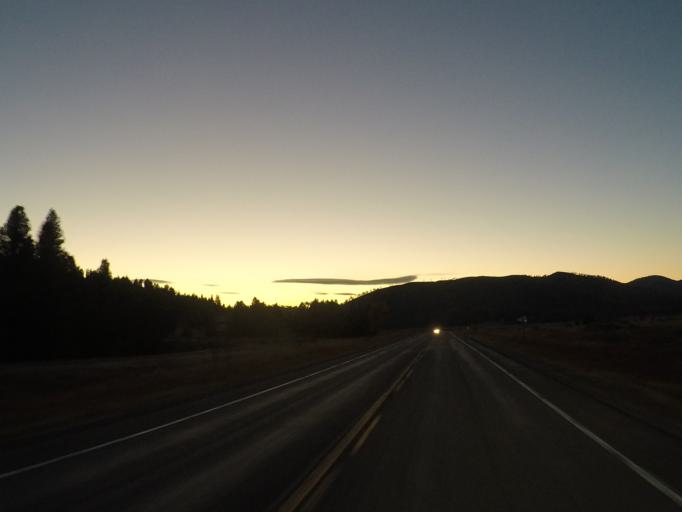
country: US
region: Montana
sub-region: Missoula County
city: Seeley Lake
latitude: 47.0295
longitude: -113.2457
